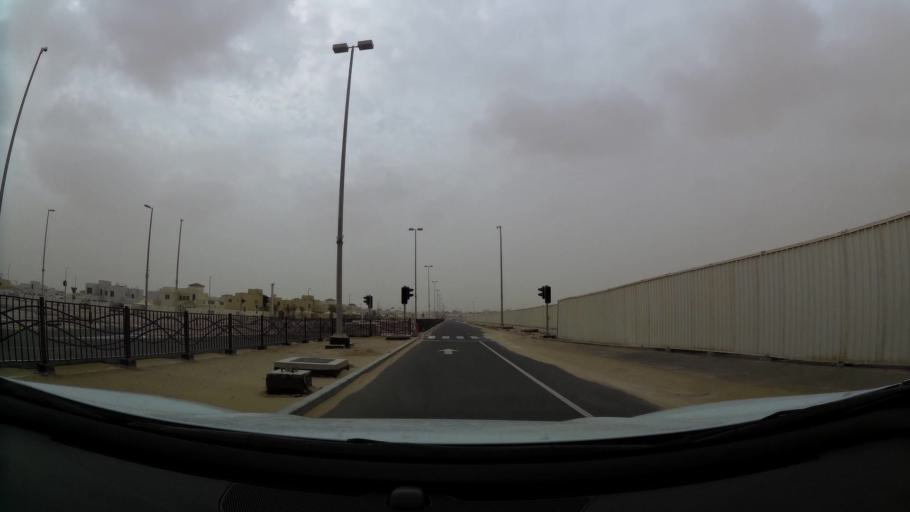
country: AE
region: Abu Dhabi
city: Abu Dhabi
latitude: 24.4370
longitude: 54.7271
